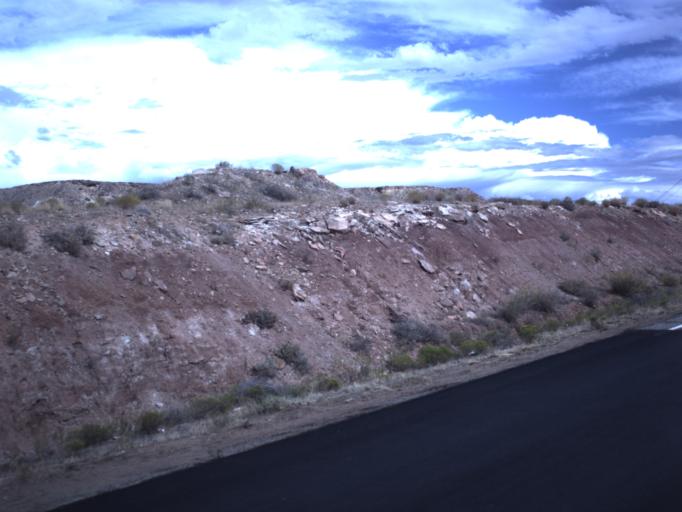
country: US
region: Colorado
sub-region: Montezuma County
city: Towaoc
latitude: 37.2174
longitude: -109.1894
